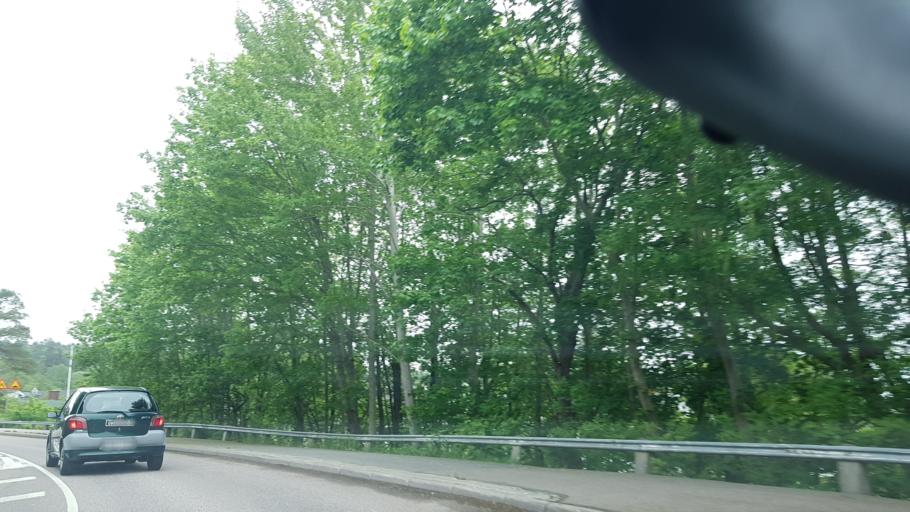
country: SE
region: Vaestra Goetaland
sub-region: Goteborg
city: Billdal
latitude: 57.6134
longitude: 11.9405
